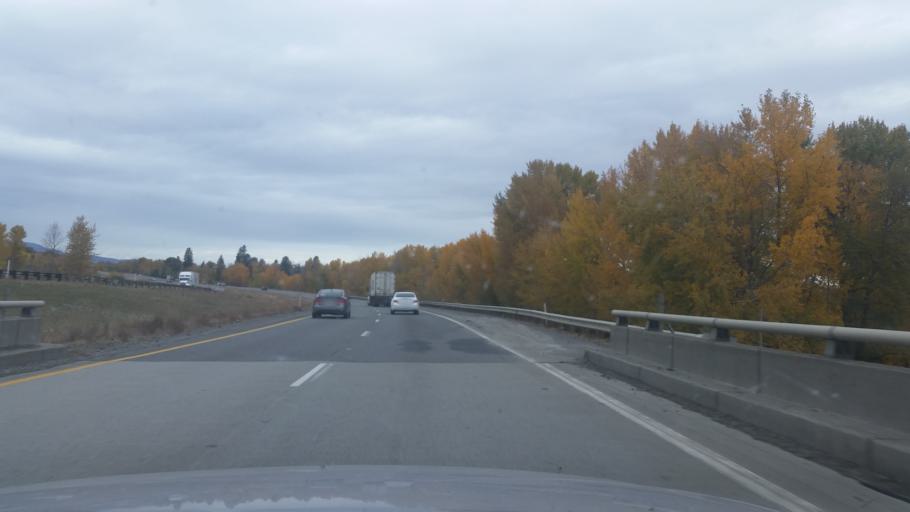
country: US
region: Washington
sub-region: Kittitas County
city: Ellensburg
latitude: 47.0385
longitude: -120.6274
